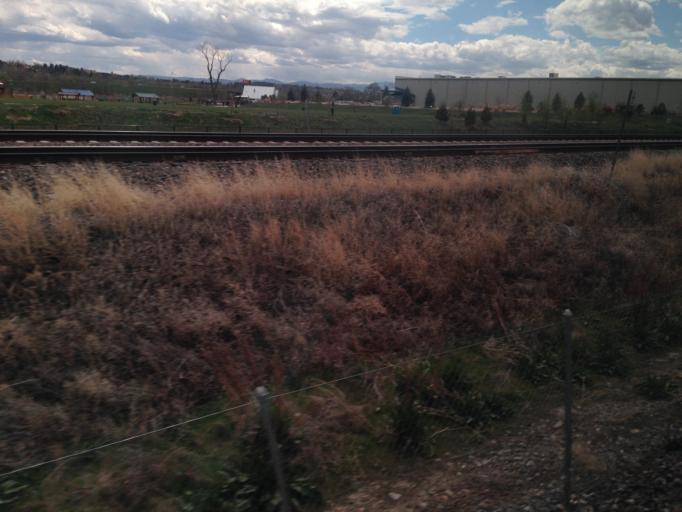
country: US
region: Colorado
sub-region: Adams County
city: Berkley
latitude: 39.8048
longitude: -105.0391
